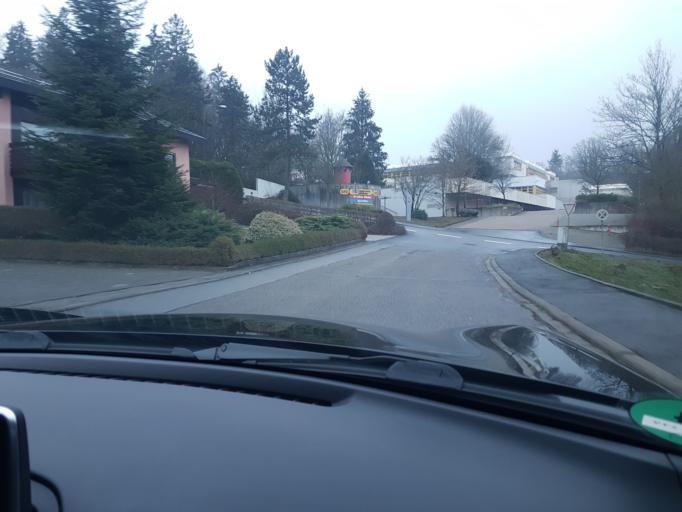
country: DE
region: Baden-Wuerttemberg
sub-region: Karlsruhe Region
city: Osterburken
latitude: 49.4307
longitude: 9.4145
